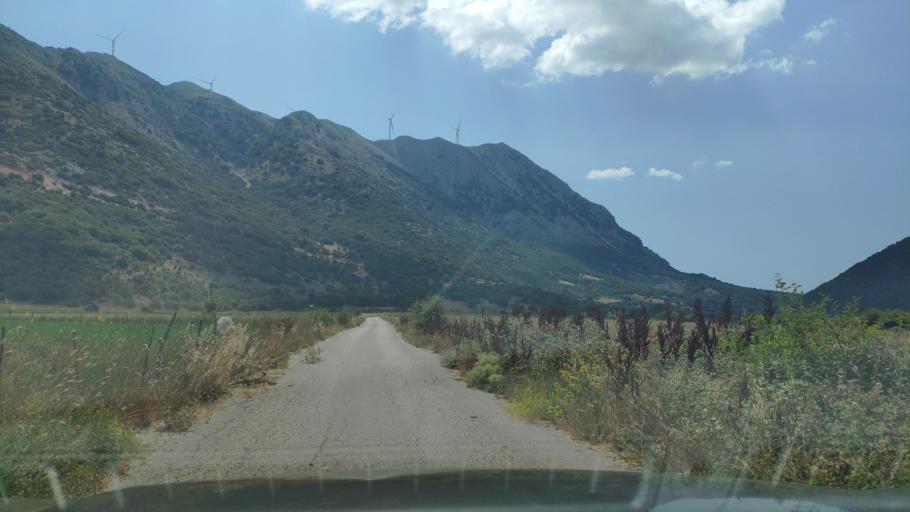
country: GR
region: West Greece
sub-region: Nomos Aitolias kai Akarnanias
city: Monastirakion
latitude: 38.7831
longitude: 20.9691
